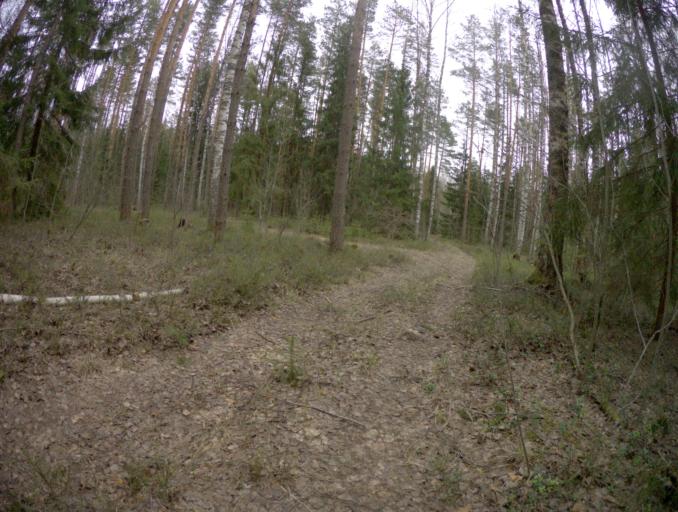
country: RU
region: Vladimir
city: Raduzhnyy
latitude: 55.9264
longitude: 40.2683
